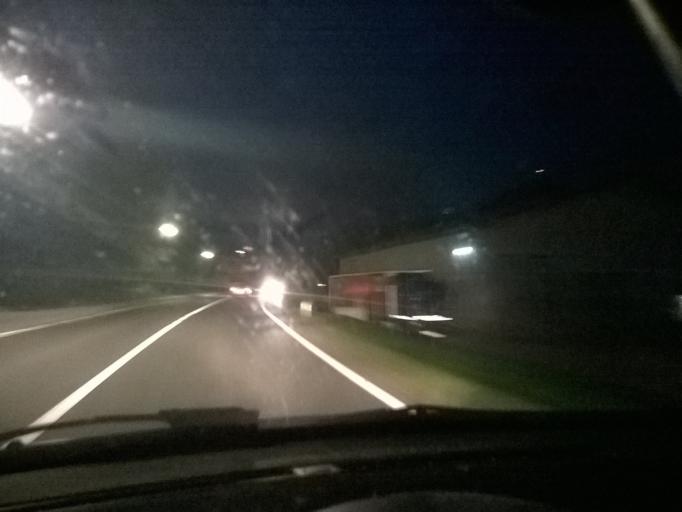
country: SI
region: Rogatec
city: Rogatec
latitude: 46.2259
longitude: 15.6950
